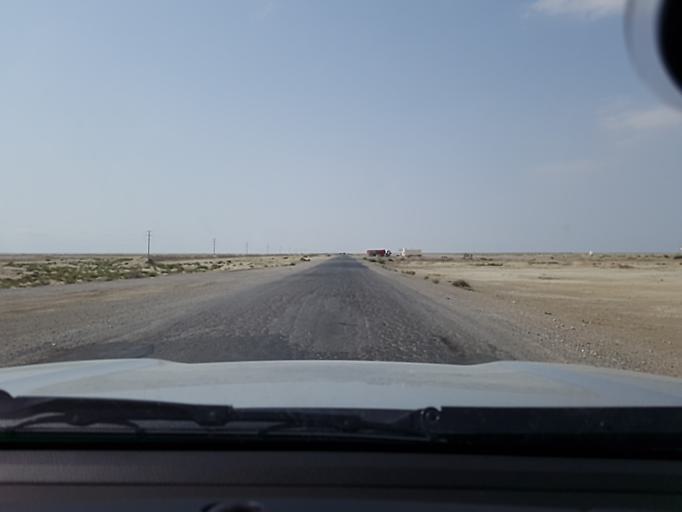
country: TM
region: Balkan
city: Gumdag
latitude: 38.9974
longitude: 54.5866
